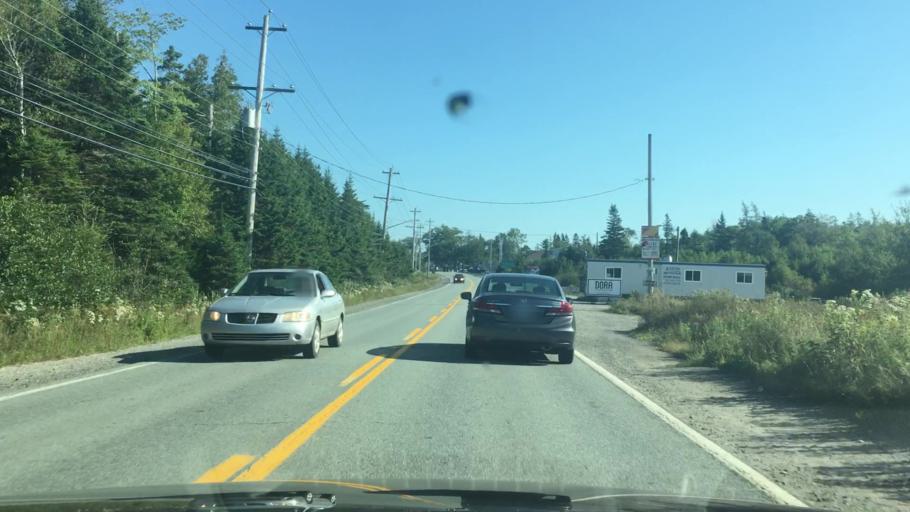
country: CA
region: Nova Scotia
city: Cole Harbour
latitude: 44.7847
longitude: -63.1510
